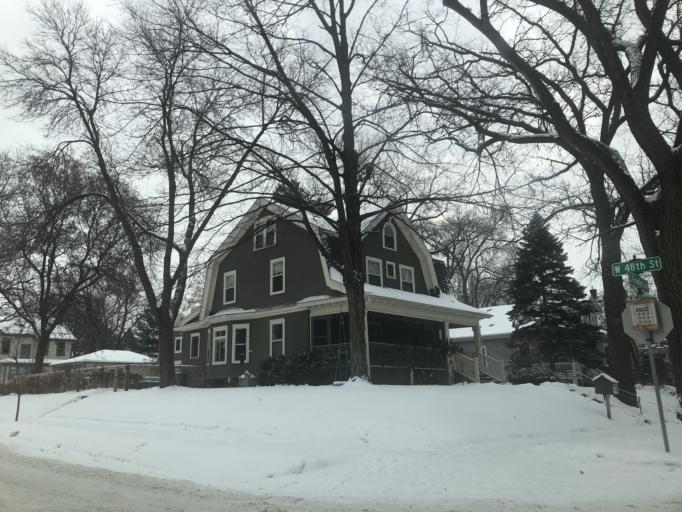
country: US
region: Minnesota
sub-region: Hennepin County
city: Richfield
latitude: 44.9160
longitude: -93.2960
